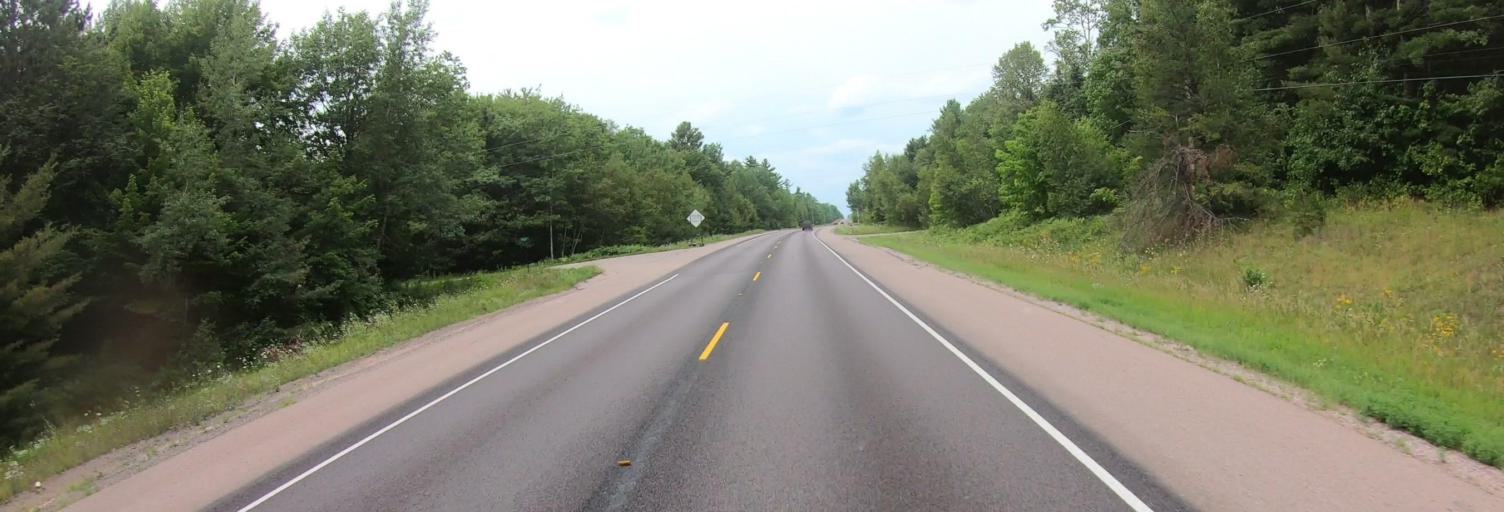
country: US
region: Michigan
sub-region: Marquette County
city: Marquette
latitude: 46.4689
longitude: -87.4376
